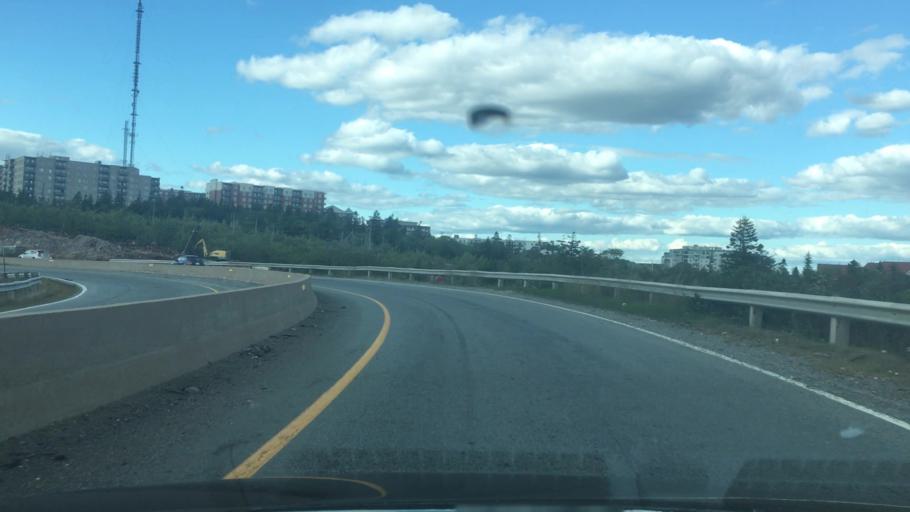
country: CA
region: Nova Scotia
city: Dartmouth
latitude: 44.6444
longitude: -63.6548
